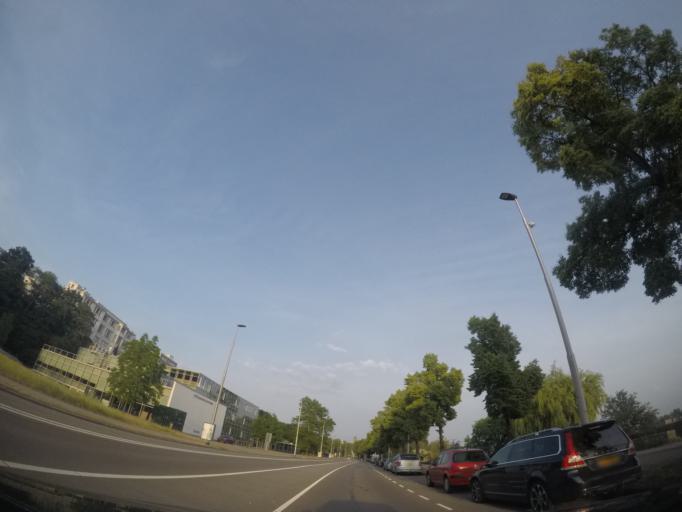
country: NL
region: Gelderland
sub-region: Gemeente Arnhem
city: Burgemeesterswijk
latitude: 51.9839
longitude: 5.8931
